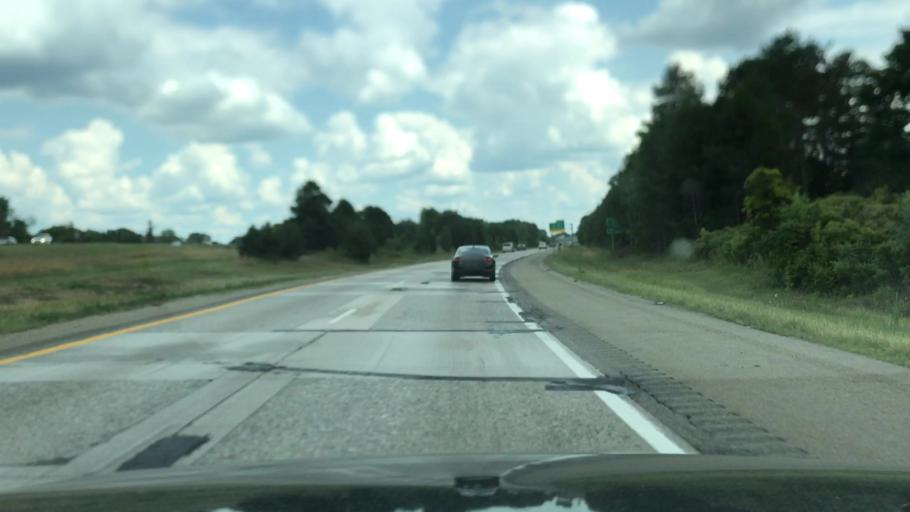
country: US
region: Michigan
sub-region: Kent County
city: East Grand Rapids
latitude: 42.9765
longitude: -85.6073
